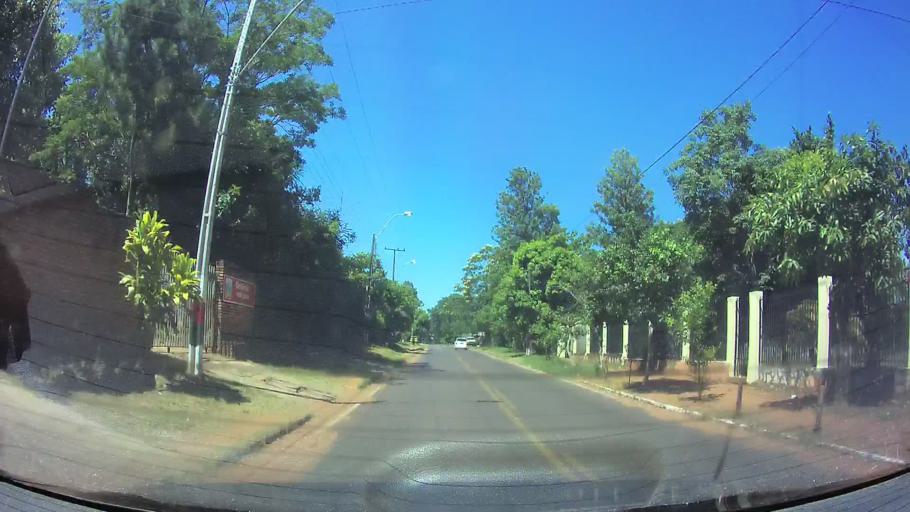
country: PY
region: Central
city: Aregua
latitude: -25.2952
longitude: -57.4143
